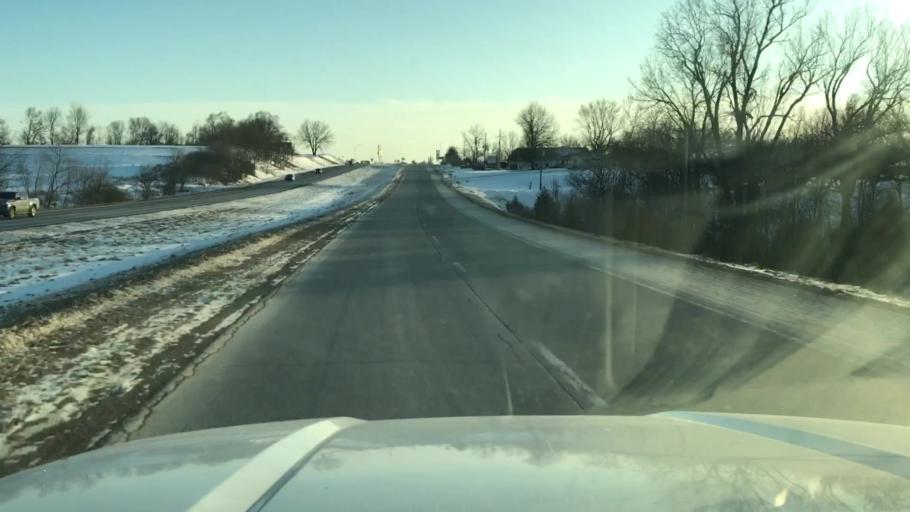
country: US
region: Missouri
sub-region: Andrew County
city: Country Club Village
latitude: 39.8640
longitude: -94.8089
